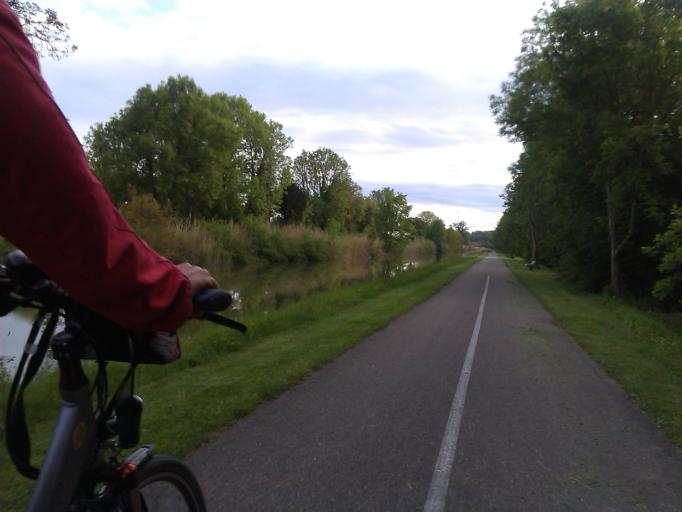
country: FR
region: Franche-Comte
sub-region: Departement du Jura
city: Dole
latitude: 47.1227
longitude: 5.5611
